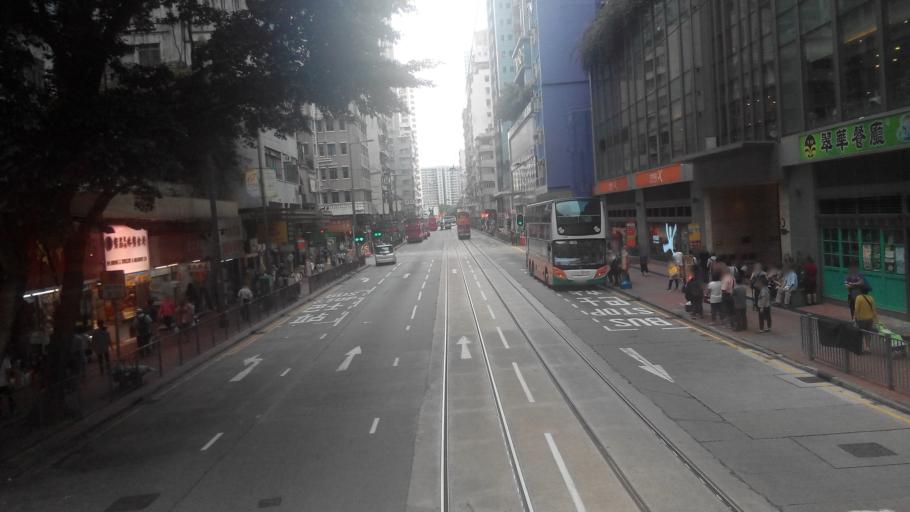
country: HK
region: Wanchai
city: Wan Chai
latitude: 22.2776
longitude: 114.2269
